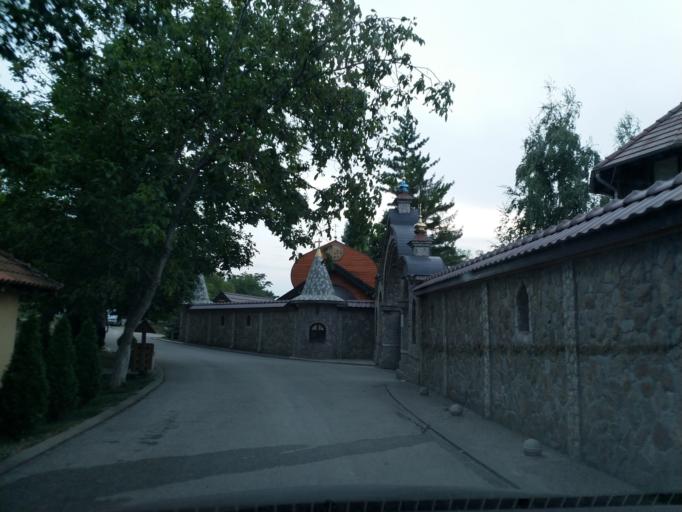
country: RS
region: Central Serbia
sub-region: Pomoravski Okrug
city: Paracin
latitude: 43.8513
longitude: 21.5355
